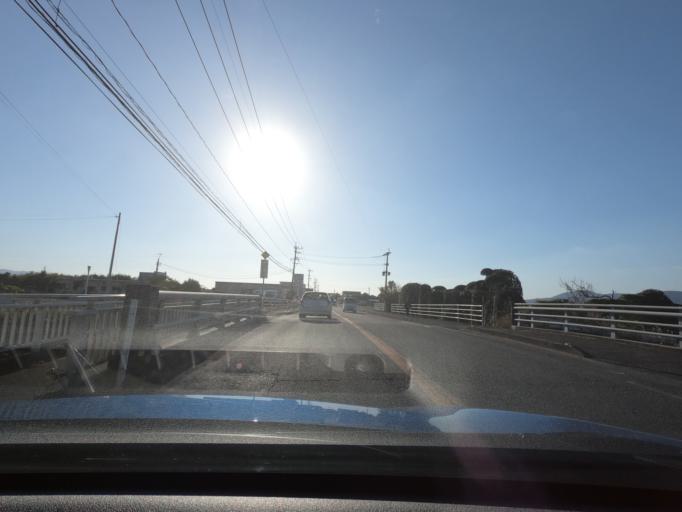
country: JP
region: Kagoshima
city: Izumi
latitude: 32.1017
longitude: 130.3109
